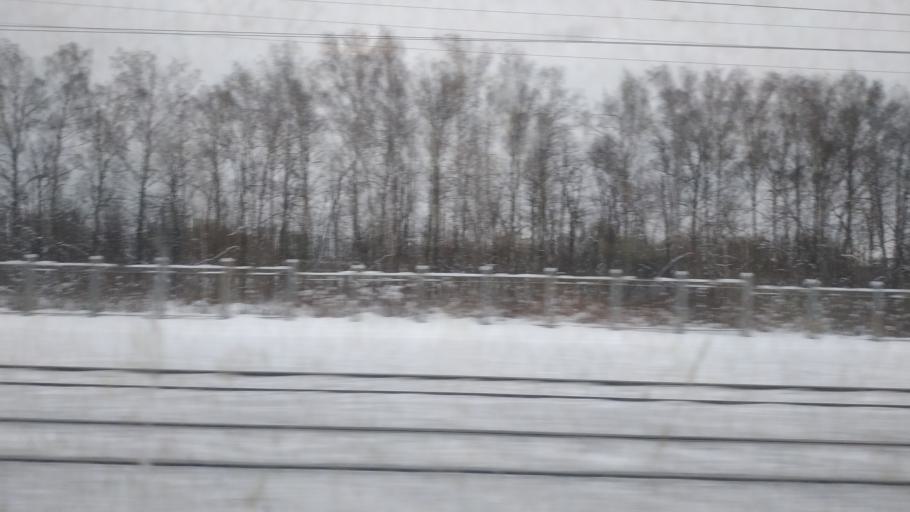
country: RU
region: Moskovskaya
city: Shcherbinka
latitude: 55.5241
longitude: 37.5663
